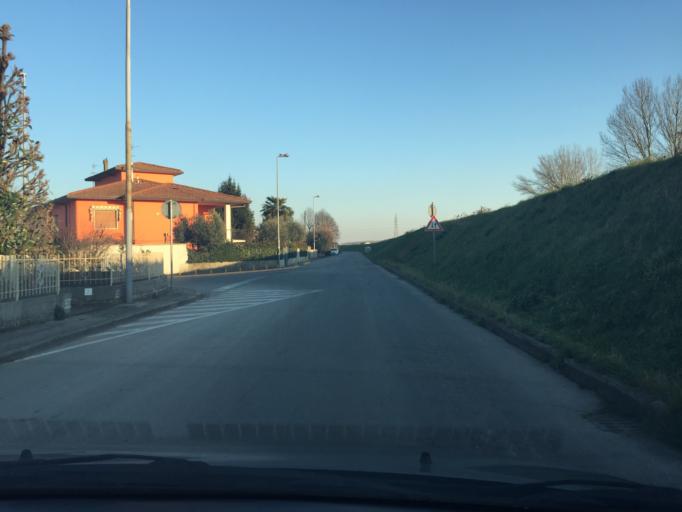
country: IT
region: Tuscany
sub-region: Provincia di Pistoia
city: Ponte Buggianese
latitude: 43.8391
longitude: 10.7510
